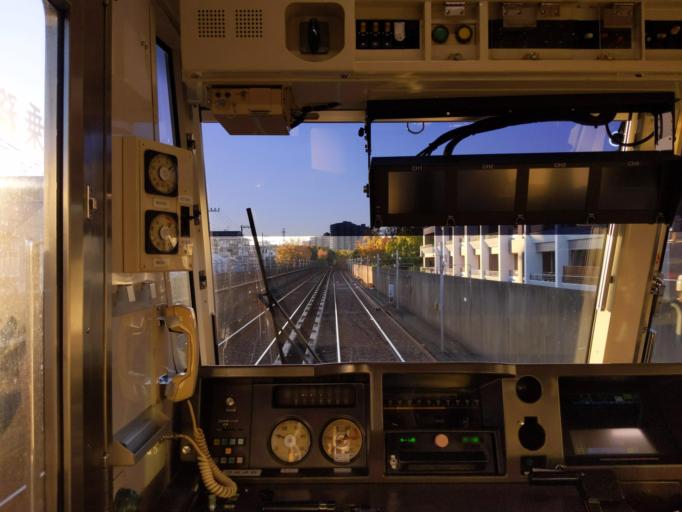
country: JP
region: Kanagawa
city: Yokohama
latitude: 35.5378
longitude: 139.5776
